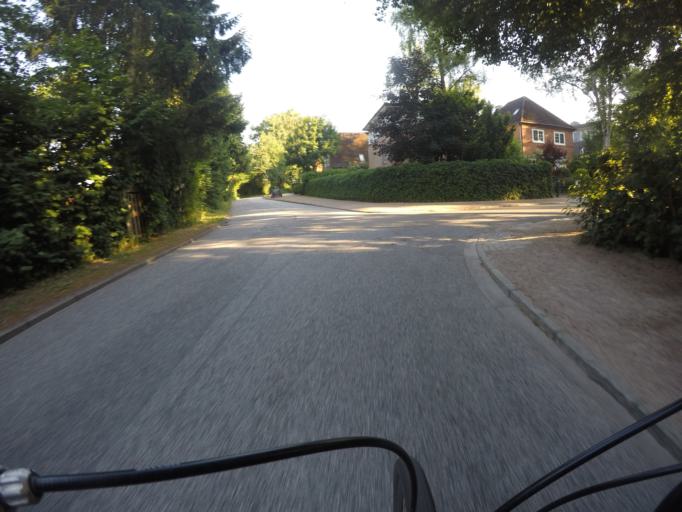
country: DE
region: Schleswig-Holstein
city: Halstenbek
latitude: 53.5694
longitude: 9.8198
